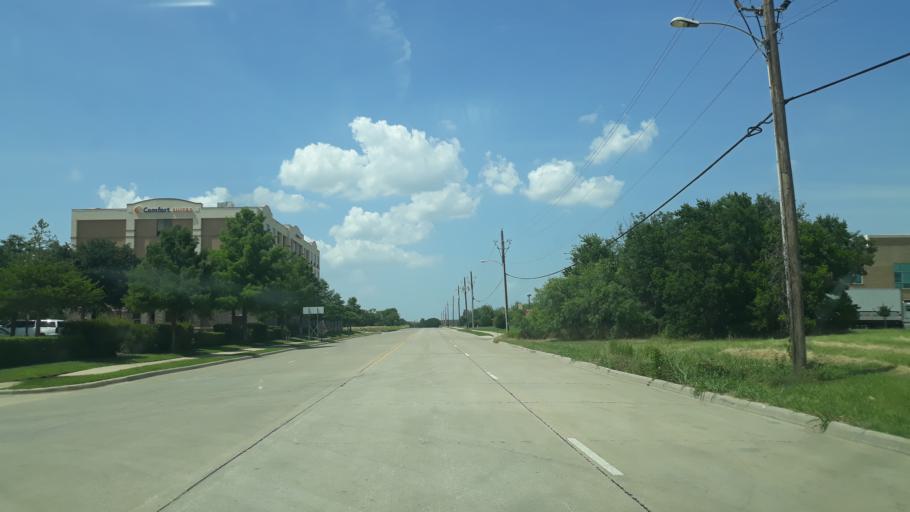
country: US
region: Texas
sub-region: Dallas County
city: Coppell
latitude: 32.9557
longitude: -97.0365
